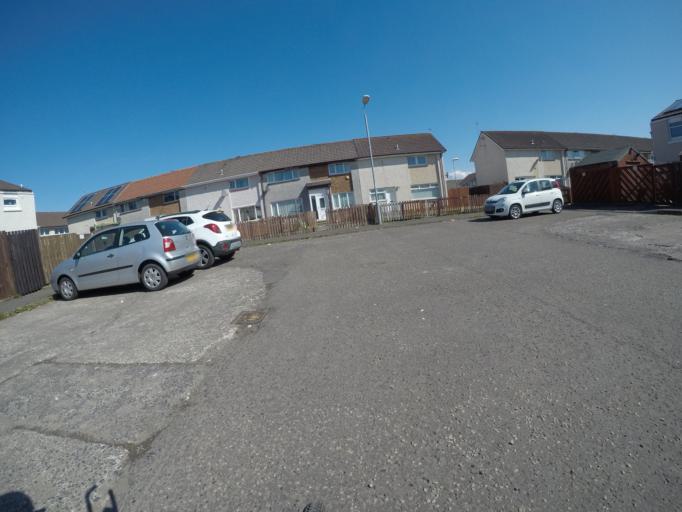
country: GB
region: Scotland
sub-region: North Ayrshire
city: Irvine
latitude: 55.6333
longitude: -4.6628
